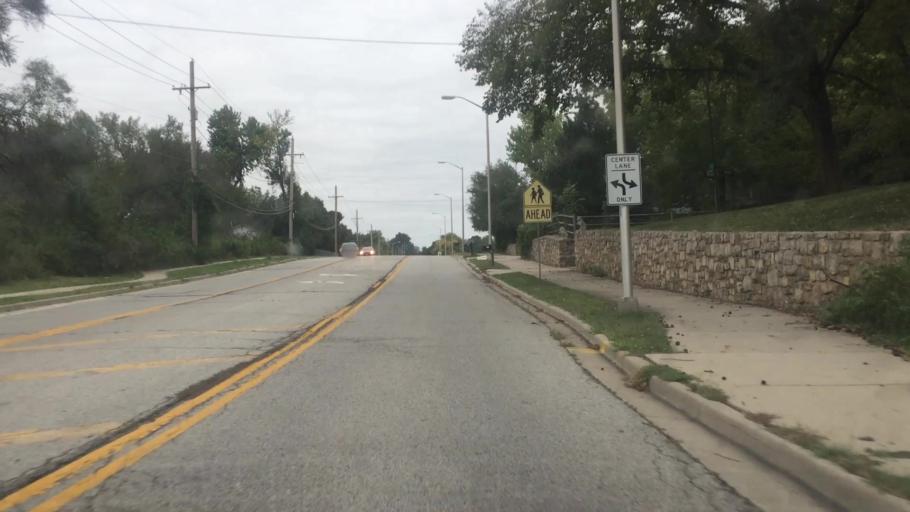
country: US
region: Kansas
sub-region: Johnson County
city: Lenexa
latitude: 38.9993
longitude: -94.7705
